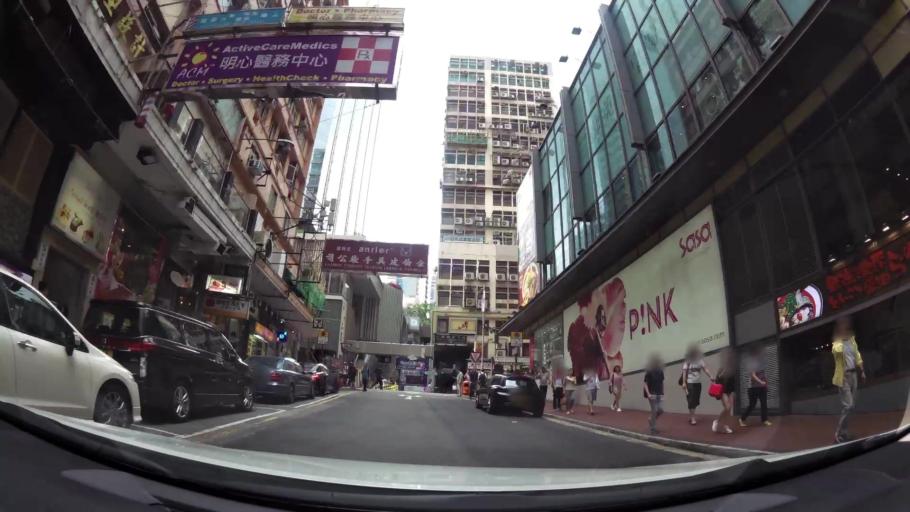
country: HK
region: Wanchai
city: Wan Chai
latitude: 22.2997
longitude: 114.1734
